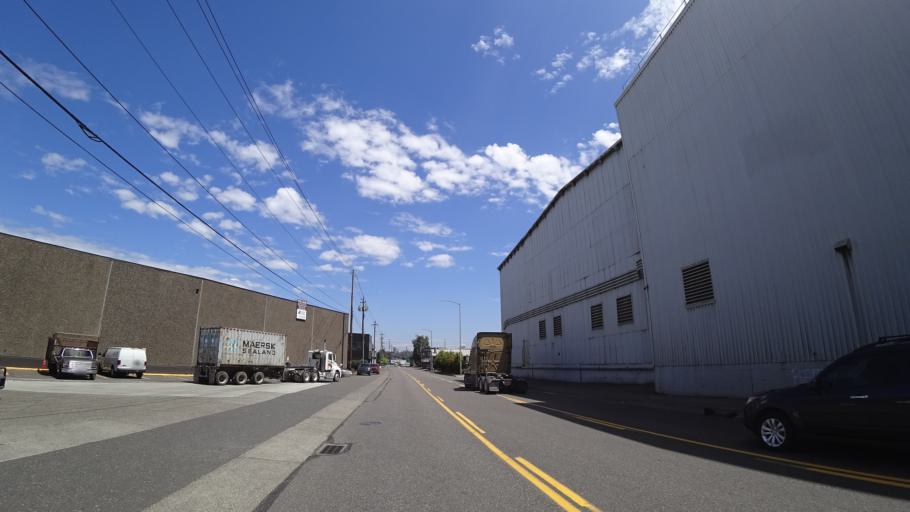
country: US
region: Oregon
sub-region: Multnomah County
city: Portland
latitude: 45.5405
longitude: -122.7028
